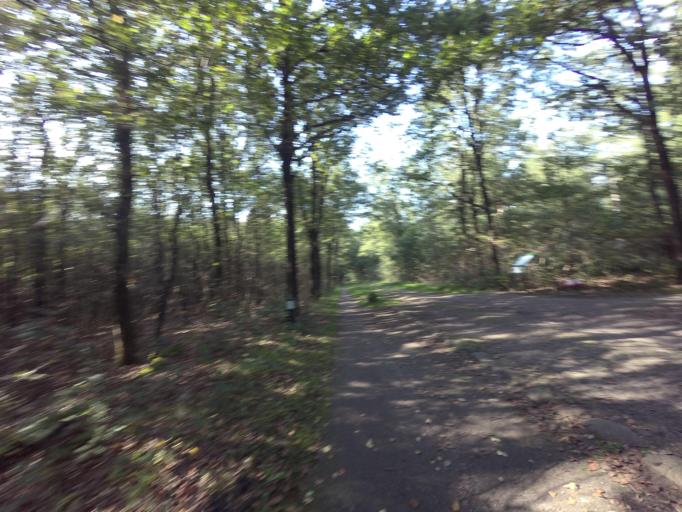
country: NL
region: Drenthe
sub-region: Gemeente Tynaarlo
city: Vries
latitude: 53.0748
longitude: 6.5114
